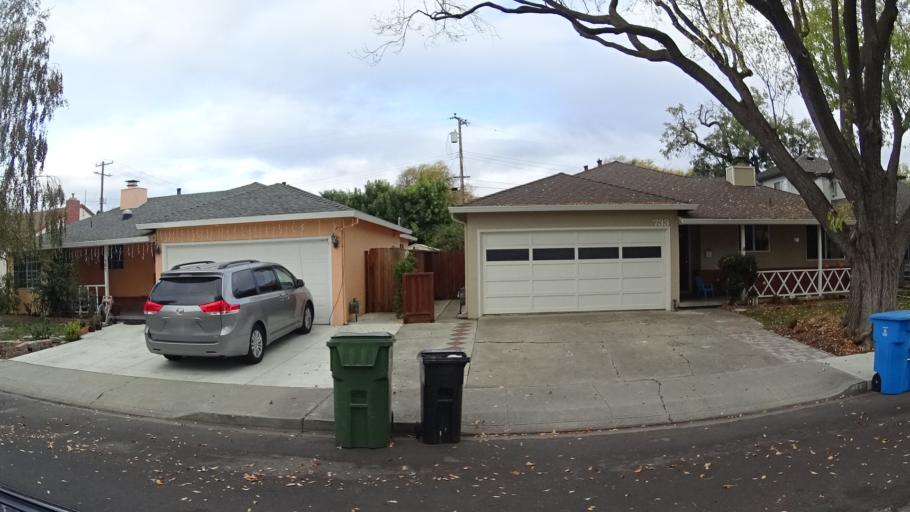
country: US
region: California
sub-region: Santa Clara County
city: Santa Clara
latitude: 37.3377
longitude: -121.9723
